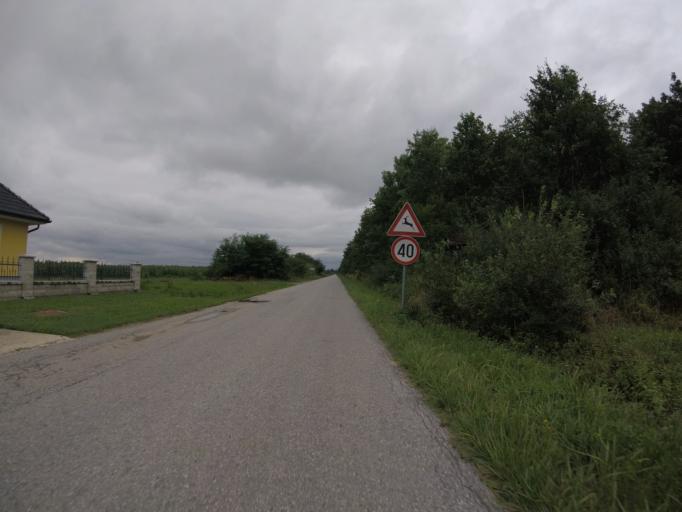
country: HR
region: Zagrebacka
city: Turopolje
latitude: 45.6380
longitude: 16.1239
